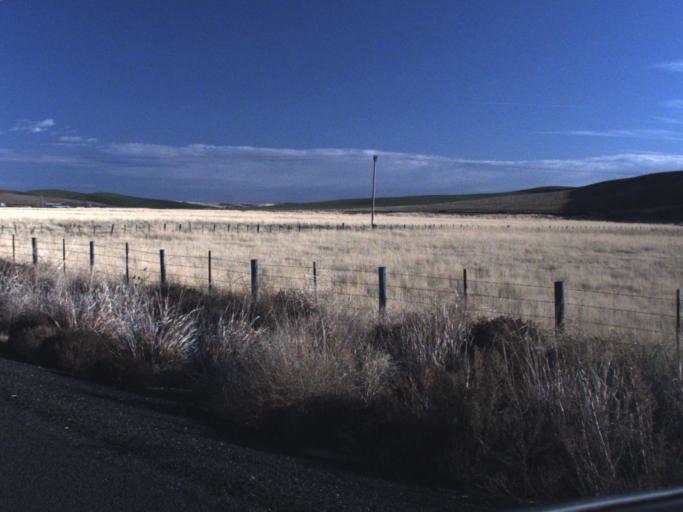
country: US
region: Washington
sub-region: Garfield County
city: Pomeroy
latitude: 46.7763
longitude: -117.7028
